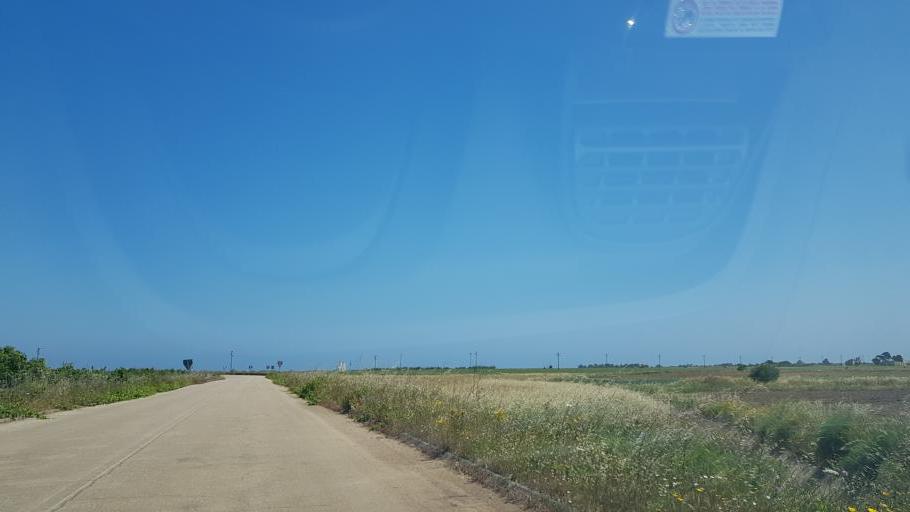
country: IT
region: Apulia
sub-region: Provincia di Brindisi
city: Brindisi
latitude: 40.6782
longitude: 17.8450
